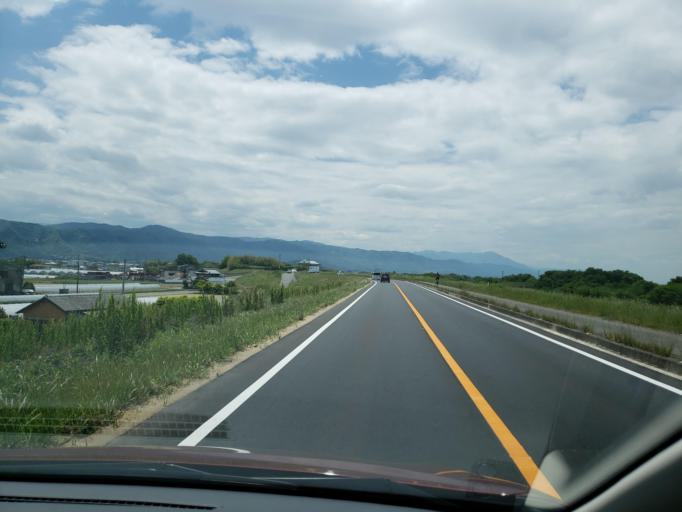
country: JP
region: Tokushima
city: Ishii
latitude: 34.0944
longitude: 134.4181
